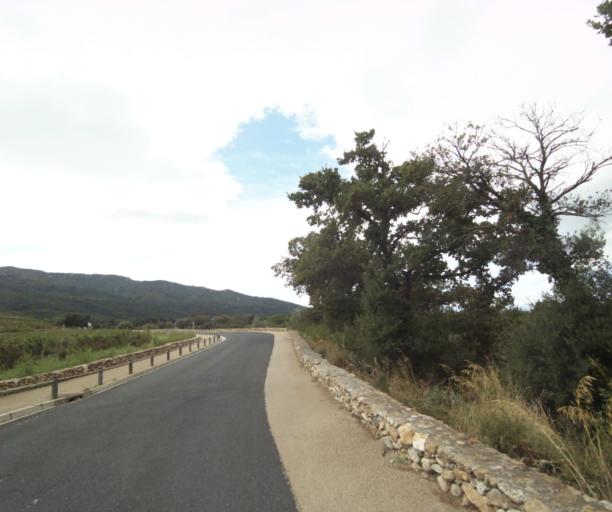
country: FR
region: Languedoc-Roussillon
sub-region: Departement des Pyrenees-Orientales
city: Argelers
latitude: 42.5340
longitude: 3.0297
